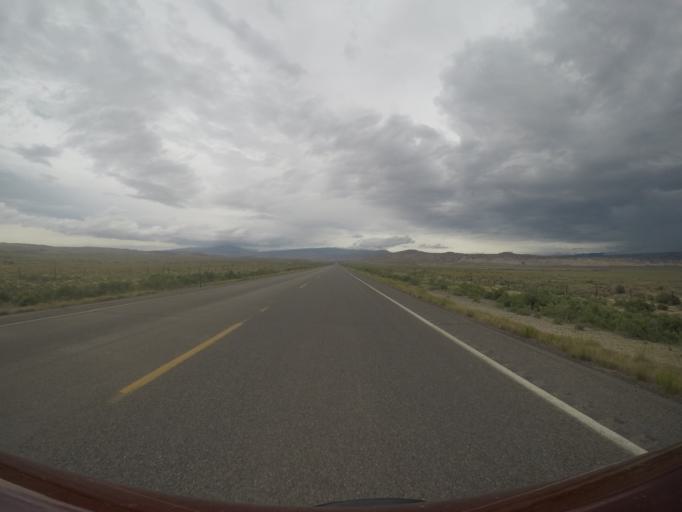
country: US
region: Wyoming
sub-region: Big Horn County
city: Lovell
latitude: 44.8956
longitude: -108.2892
